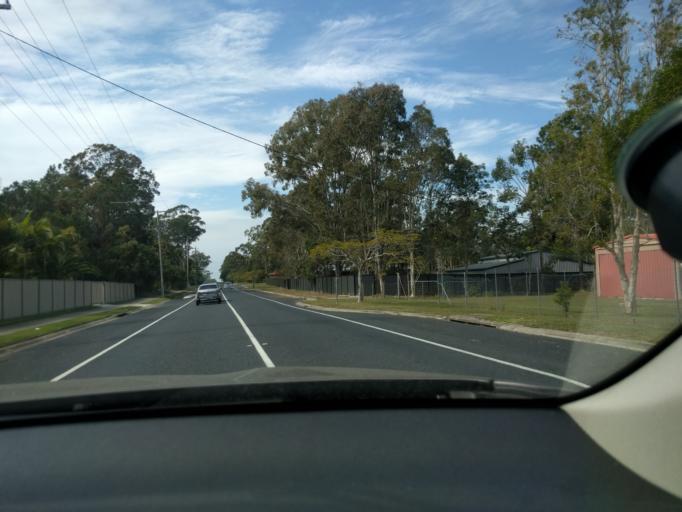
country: AU
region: Queensland
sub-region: Moreton Bay
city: Burpengary
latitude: -27.1406
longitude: 152.9922
